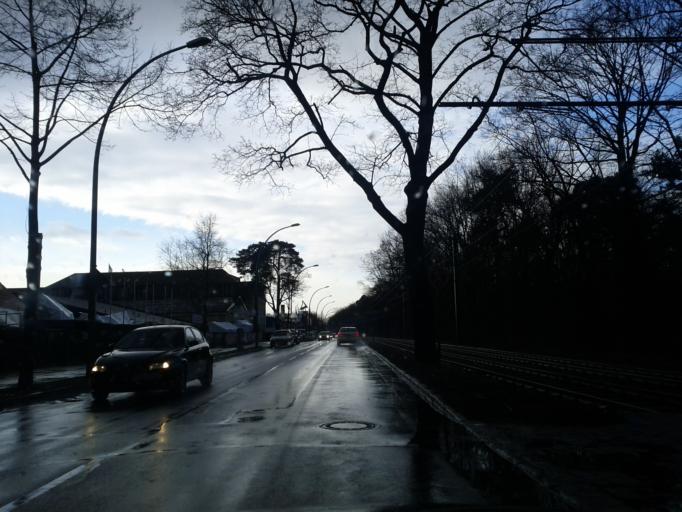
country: DE
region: Berlin
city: Friedrichshagen
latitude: 52.4481
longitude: 13.6120
